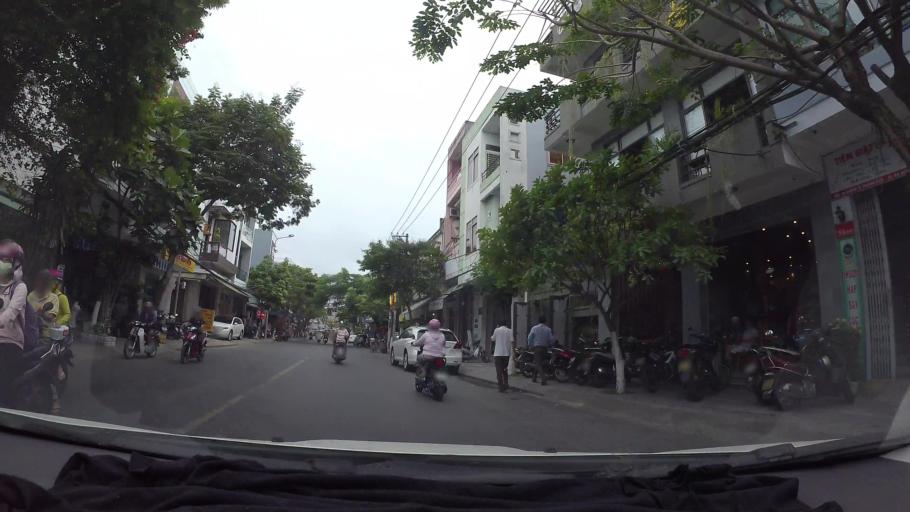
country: VN
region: Da Nang
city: Thanh Khe
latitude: 16.0686
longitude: 108.1815
